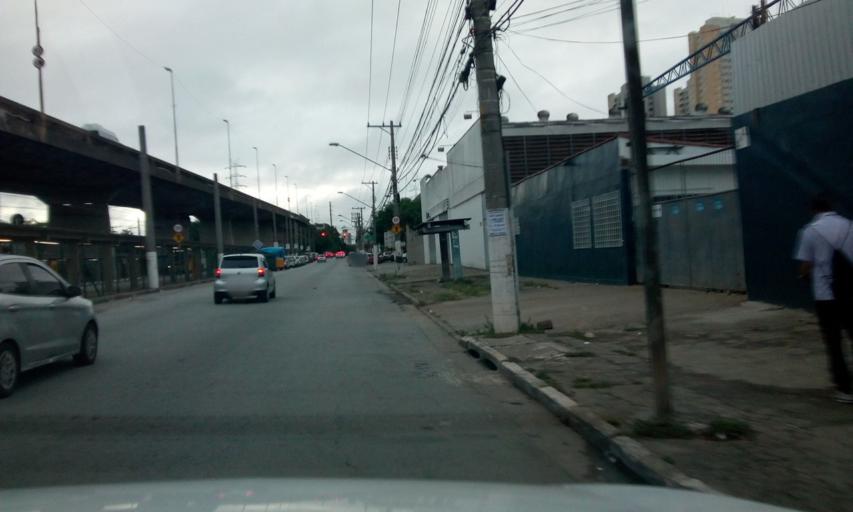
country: BR
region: Sao Paulo
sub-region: Guarulhos
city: Guarulhos
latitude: -23.5278
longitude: -46.5553
